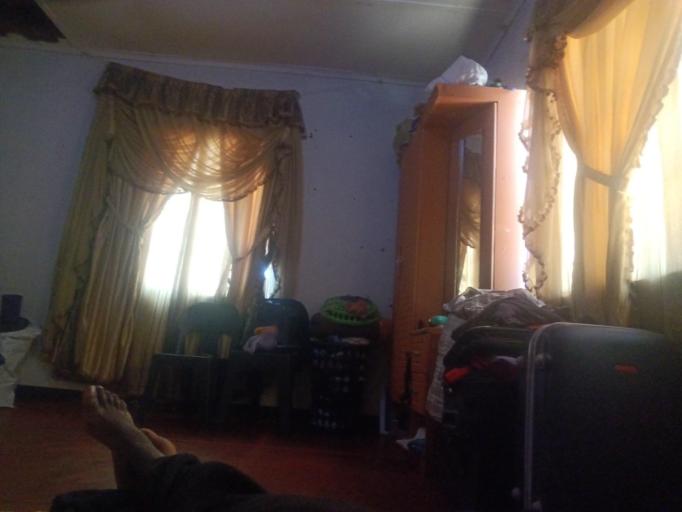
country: ZW
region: Matabeleland South
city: Gwanda
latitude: -21.3819
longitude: 28.9808
